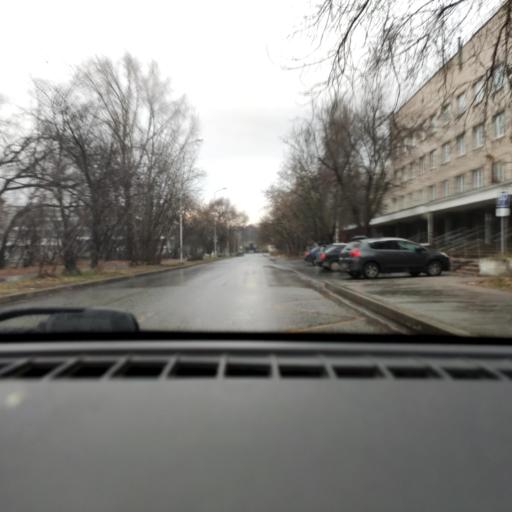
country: RU
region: Perm
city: Kultayevo
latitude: 57.9938
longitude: 55.9350
